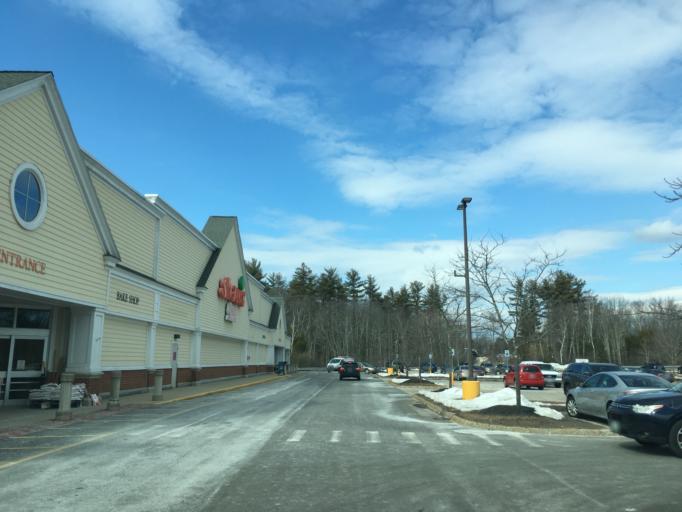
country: US
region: New Hampshire
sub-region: Rockingham County
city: Exeter
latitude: 42.9966
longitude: -70.9270
